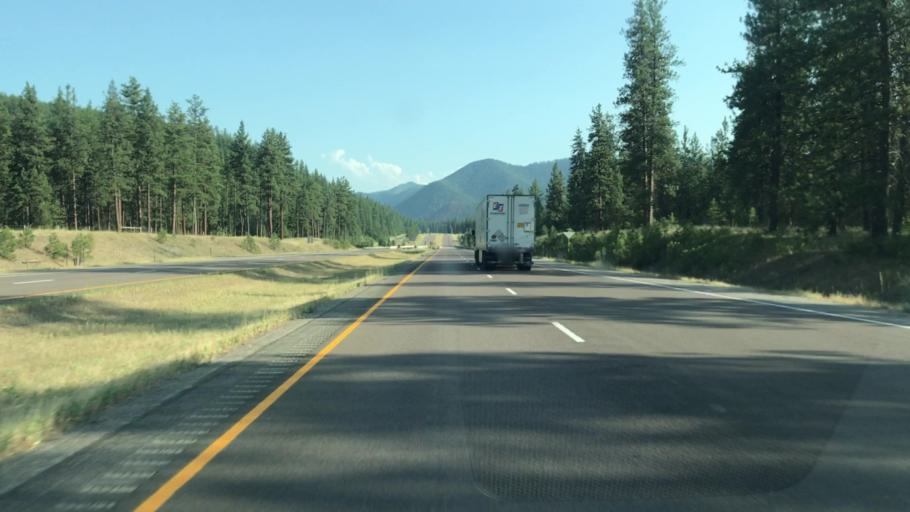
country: US
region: Montana
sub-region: Mineral County
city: Superior
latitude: 47.0725
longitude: -114.7655
